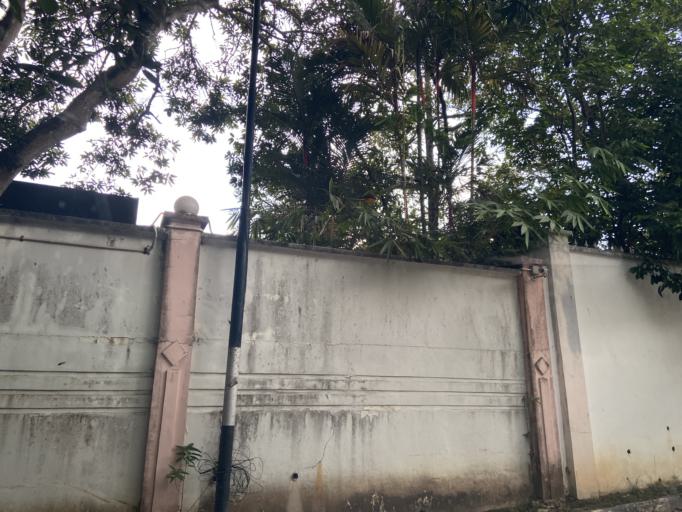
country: SG
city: Singapore
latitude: 1.1217
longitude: 104.0223
